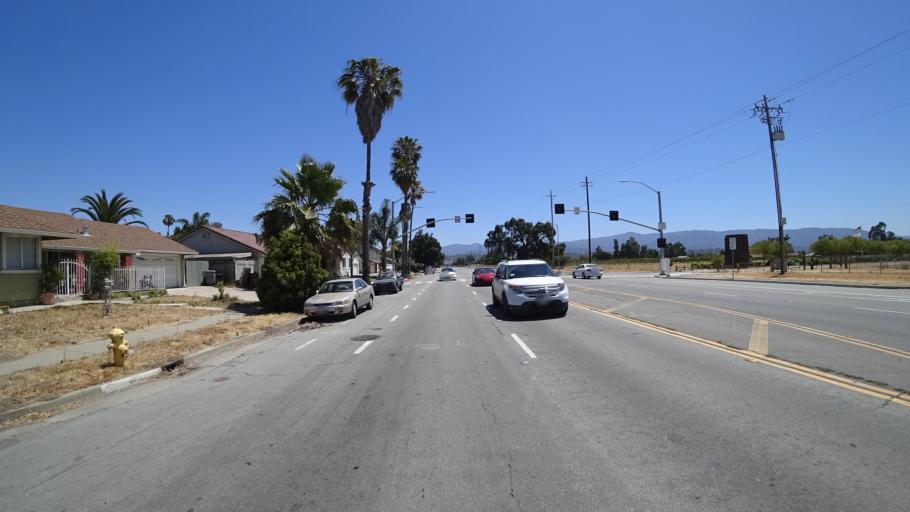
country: US
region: California
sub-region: Santa Clara County
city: Seven Trees
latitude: 37.2641
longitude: -121.8309
